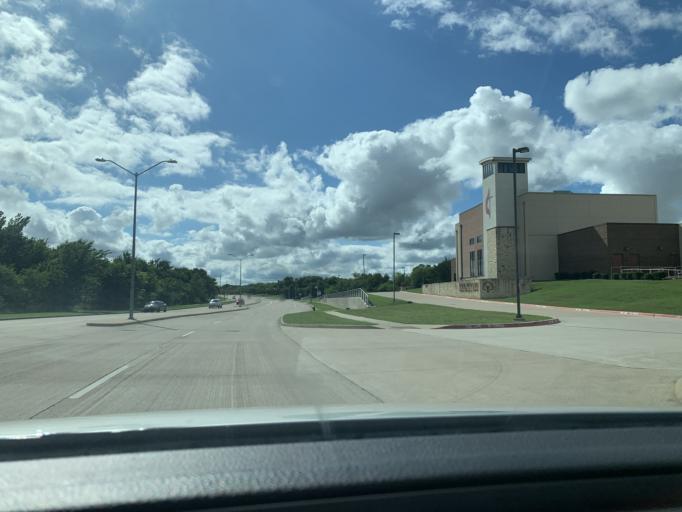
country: US
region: Texas
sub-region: Dallas County
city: Grand Prairie
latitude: 32.6674
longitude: -97.0215
